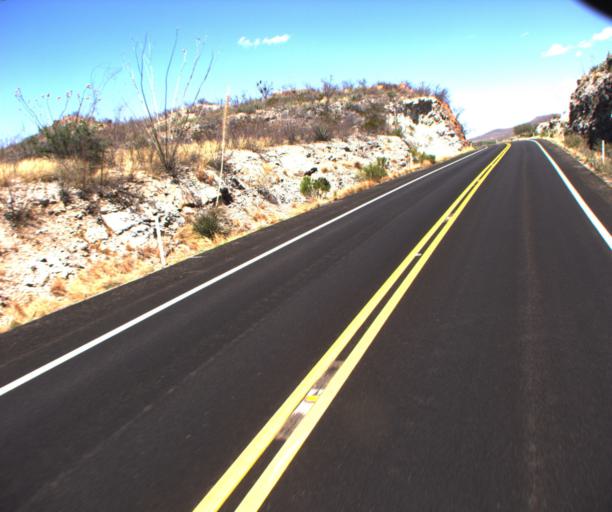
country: US
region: Arizona
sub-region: Cochise County
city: Bisbee
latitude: 31.5209
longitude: -110.0164
